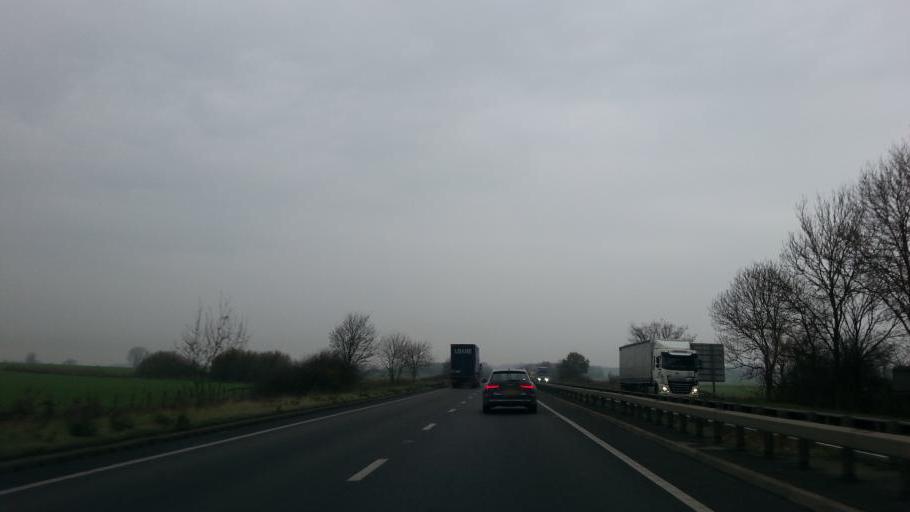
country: GB
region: England
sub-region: Cambridgeshire
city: Great Stukeley
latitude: 52.3503
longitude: -0.2233
